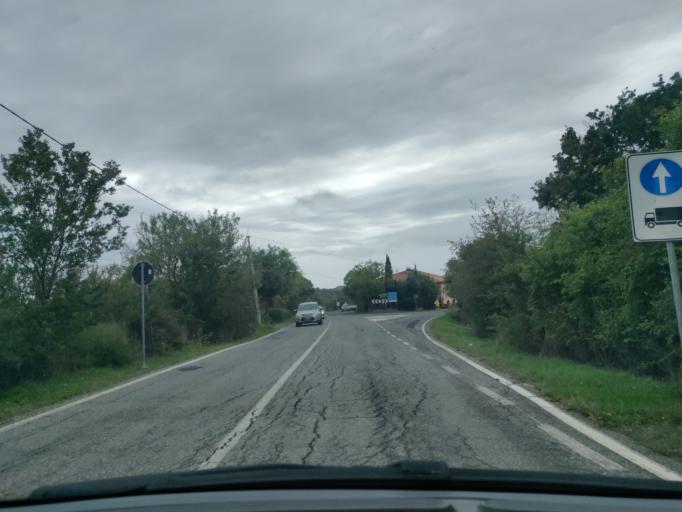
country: IT
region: Latium
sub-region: Citta metropolitana di Roma Capitale
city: Allumiere
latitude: 42.1263
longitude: 11.8648
